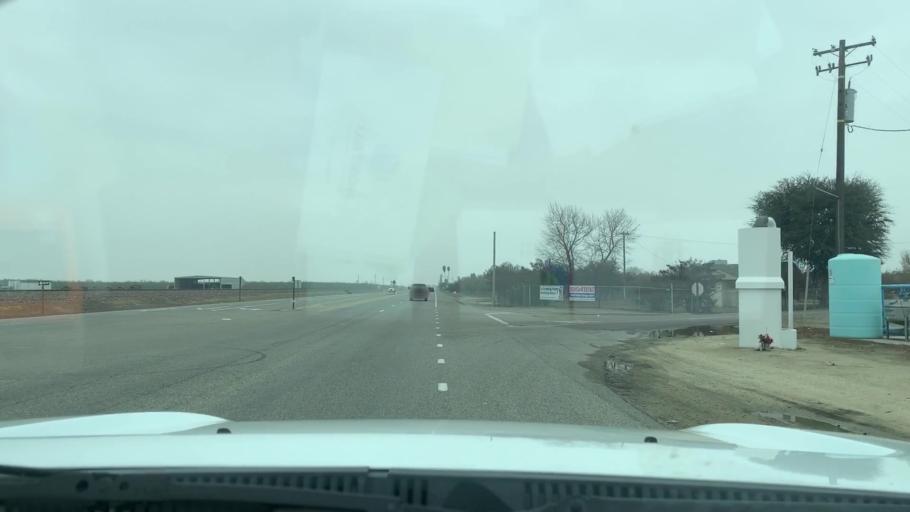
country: US
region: California
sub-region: Kern County
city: Shafter
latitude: 35.5206
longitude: -119.2960
